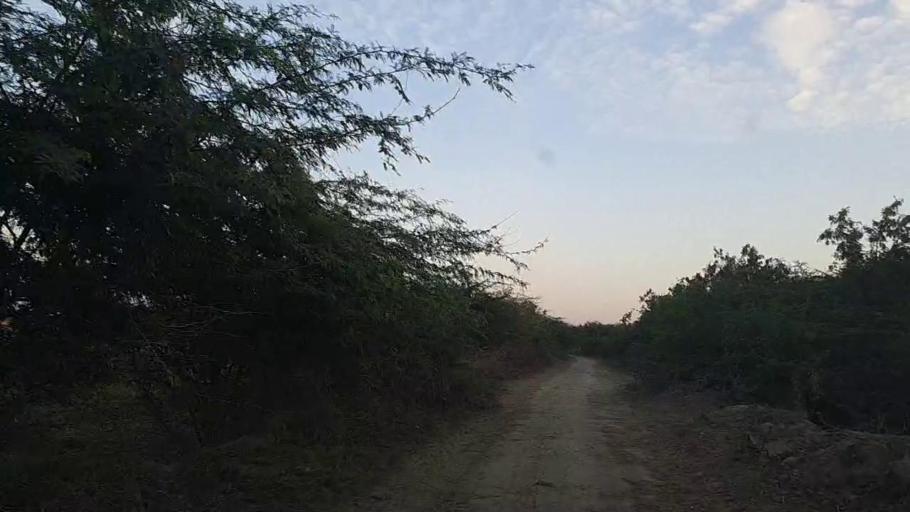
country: PK
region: Sindh
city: Thatta
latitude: 24.7939
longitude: 67.9158
